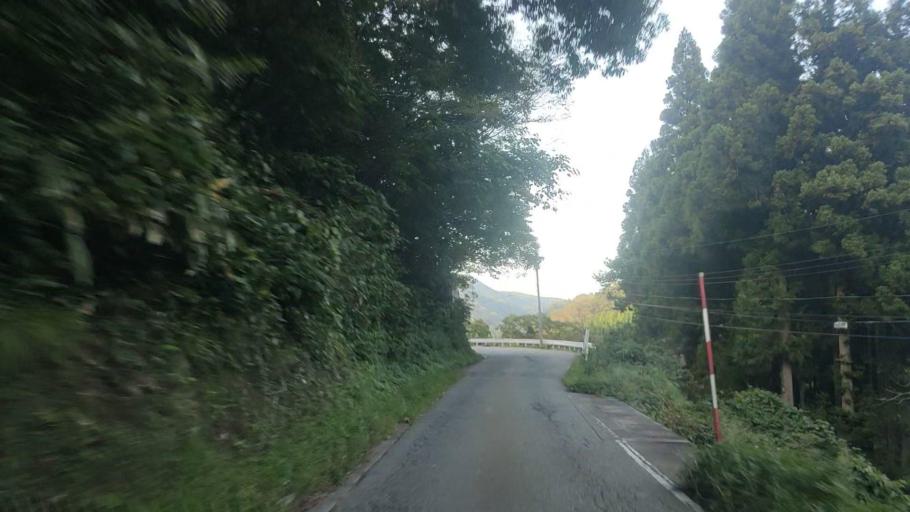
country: JP
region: Toyama
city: Yatsuomachi-higashikumisaka
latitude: 36.4993
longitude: 137.0641
